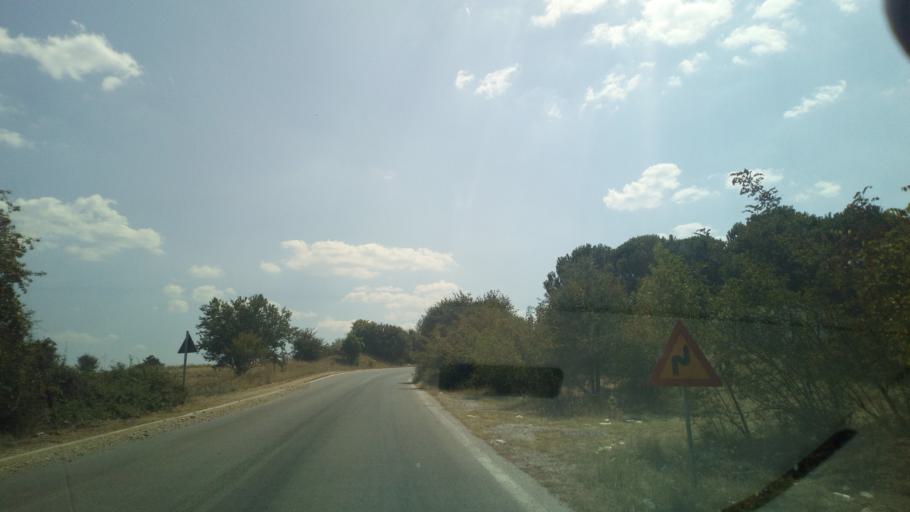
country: GR
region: Central Macedonia
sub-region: Nomos Thessalonikis
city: Agios Vasileios
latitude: 40.6550
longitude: 23.1141
